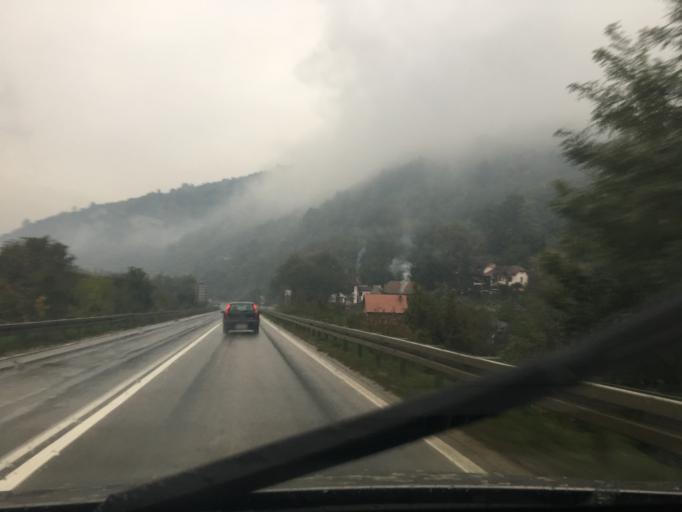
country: RS
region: Central Serbia
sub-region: Pcinjski Okrug
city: Vladicin Han
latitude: 42.7760
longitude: 22.0928
